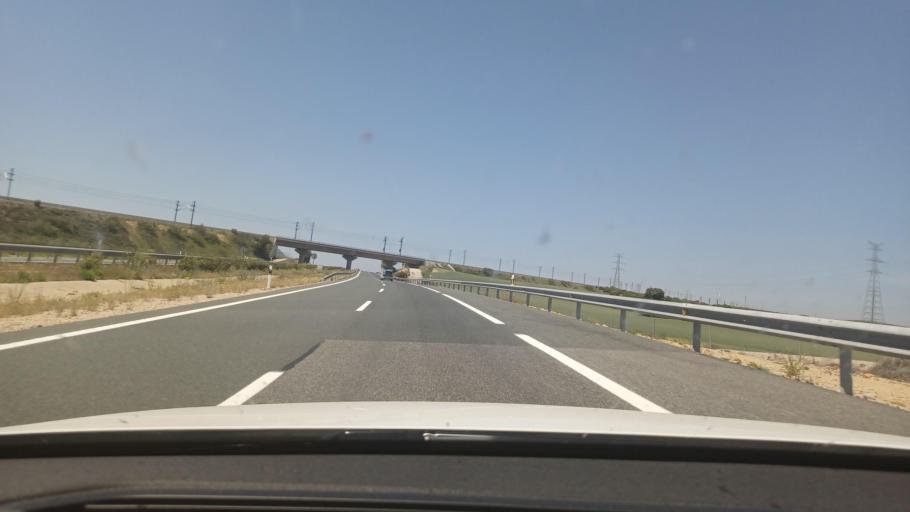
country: ES
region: Castille-La Mancha
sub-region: Provincia de Albacete
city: Alpera
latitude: 38.8805
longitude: -1.2522
